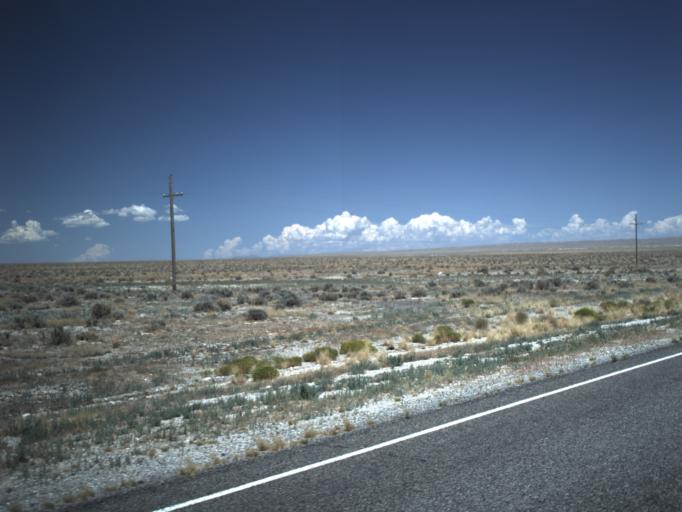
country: US
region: Utah
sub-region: Millard County
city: Delta
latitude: 39.0770
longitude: -113.2057
